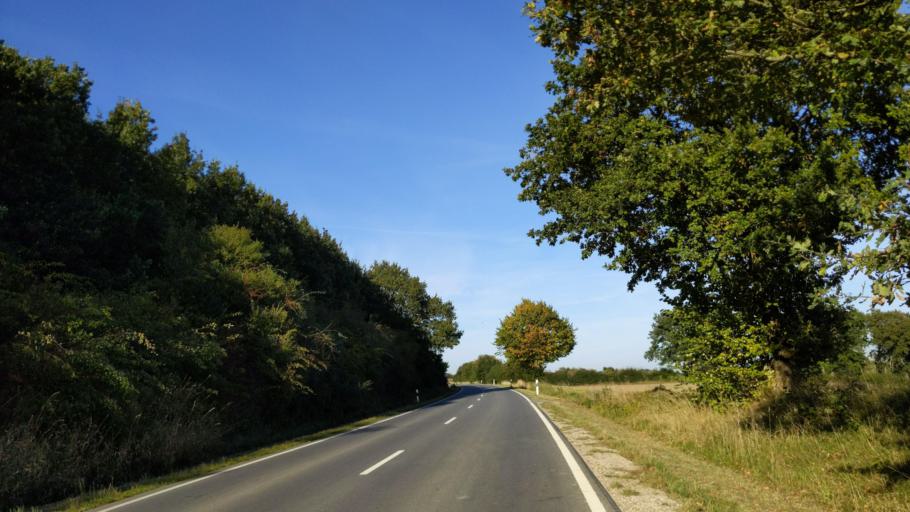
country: DE
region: Schleswig-Holstein
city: Ahrensbok
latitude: 54.0716
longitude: 10.5914
